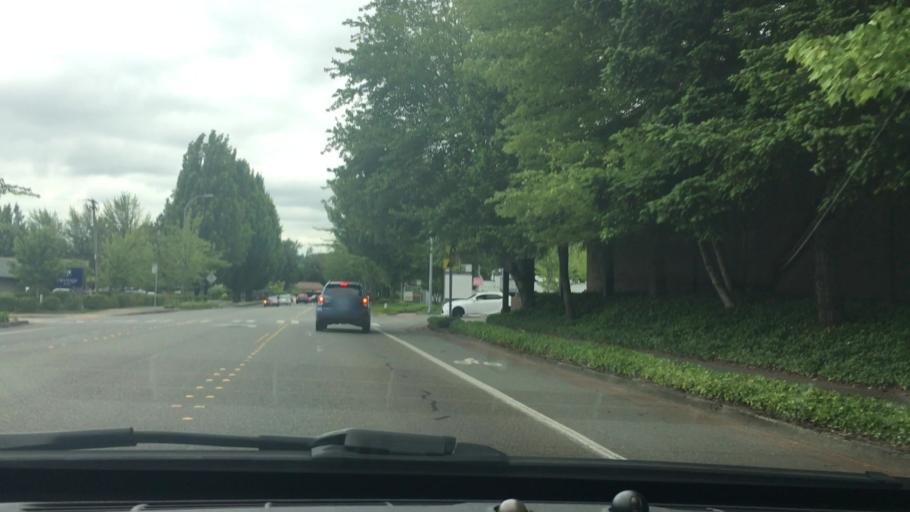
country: US
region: Washington
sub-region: King County
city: Issaquah
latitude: 47.5440
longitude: -122.0574
